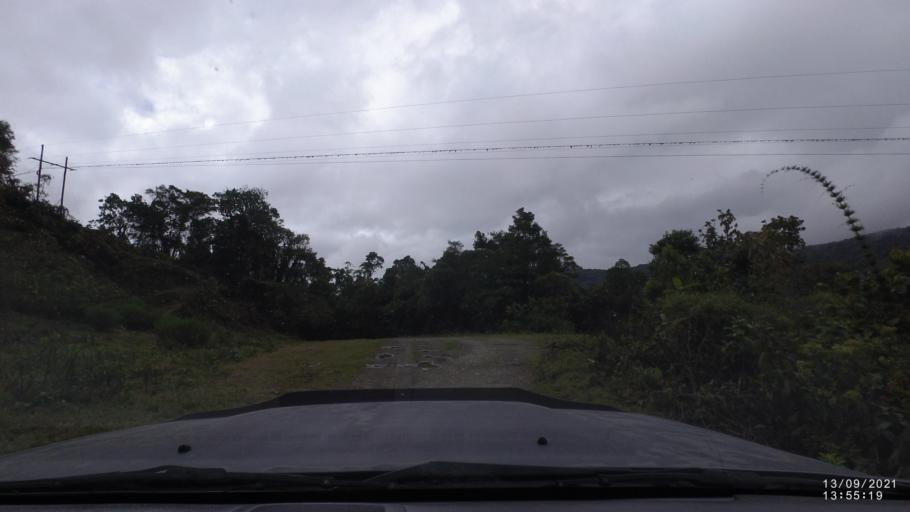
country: BO
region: Cochabamba
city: Colomi
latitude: -17.2170
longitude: -65.8619
